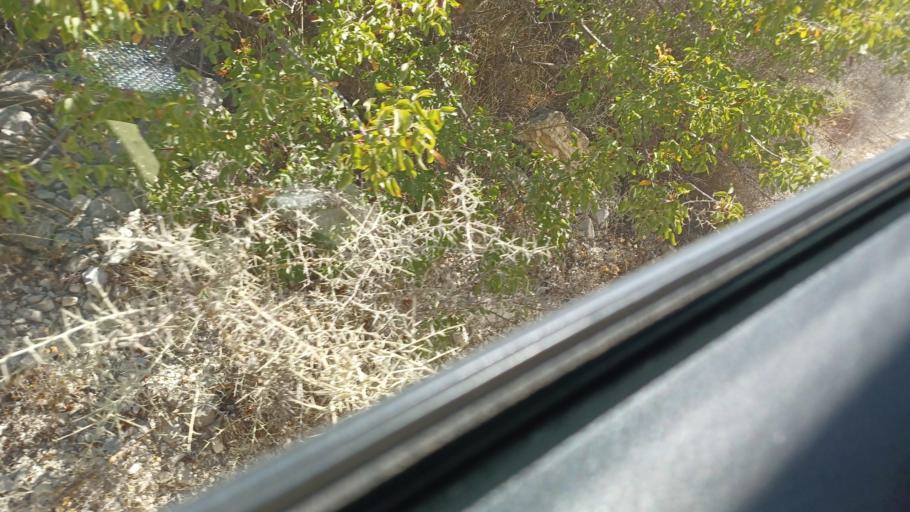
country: CY
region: Pafos
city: Tala
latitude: 34.8692
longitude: 32.4322
